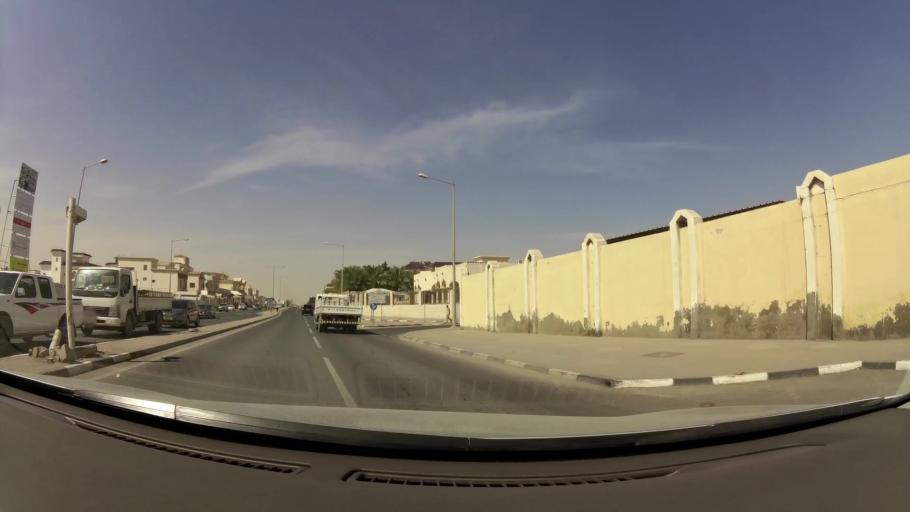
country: QA
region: Baladiyat ar Rayyan
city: Ar Rayyan
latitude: 25.2797
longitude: 51.4205
